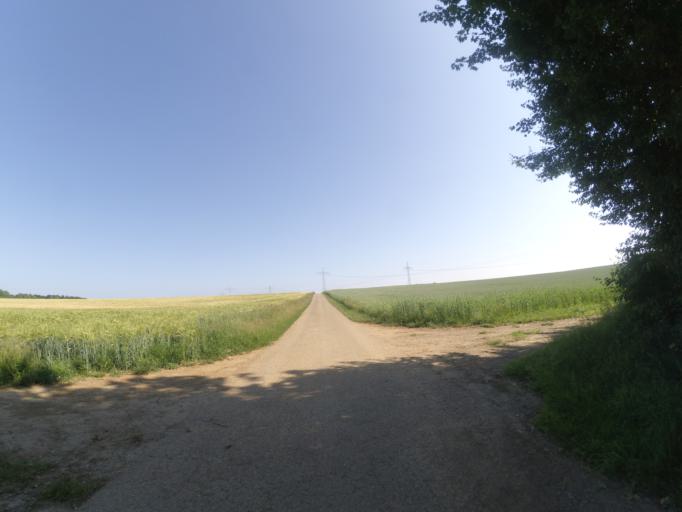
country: DE
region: Baden-Wuerttemberg
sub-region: Tuebingen Region
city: Beimerstetten
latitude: 48.4630
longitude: 9.9876
